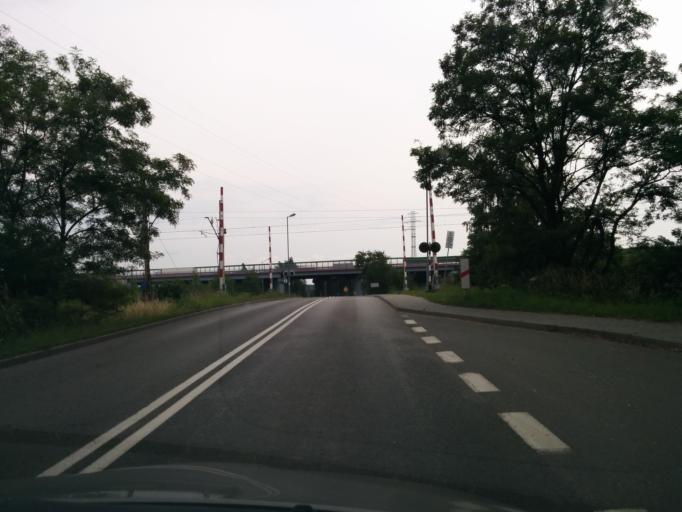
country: PL
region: Silesian Voivodeship
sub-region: Ruda Slaska
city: Ruda Slaska
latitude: 50.2595
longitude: 18.8391
